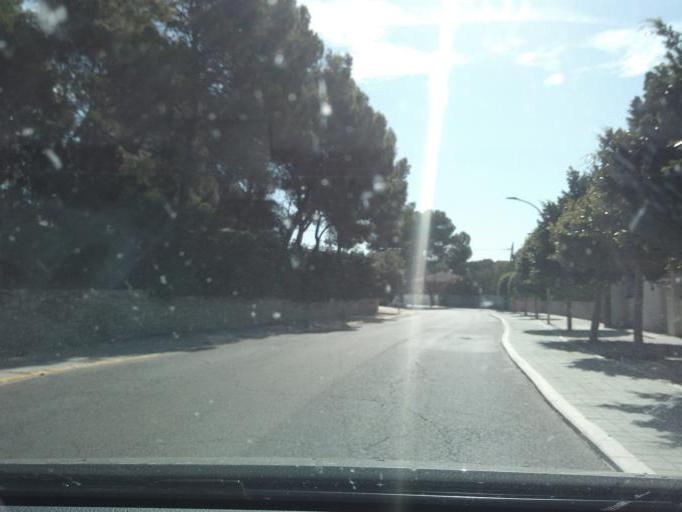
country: ES
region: Valencia
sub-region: Provincia de Valencia
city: Betera
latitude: 39.5417
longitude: -0.4848
